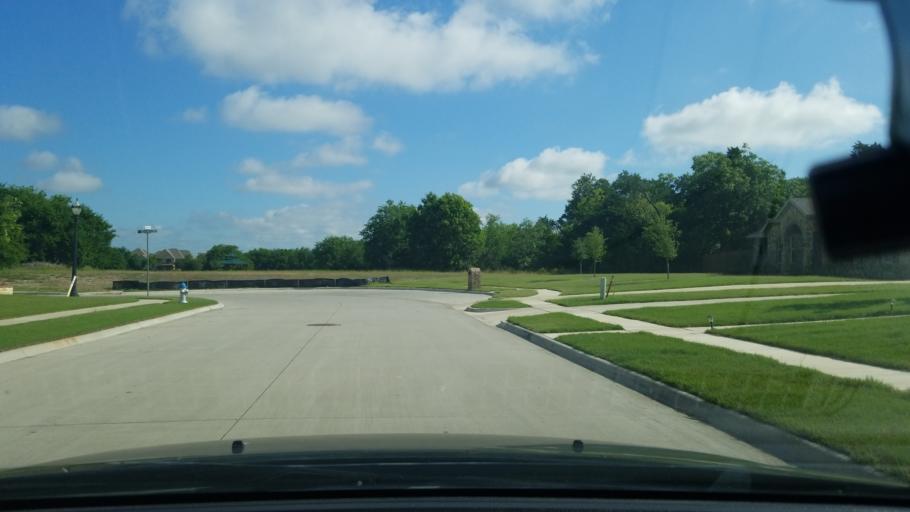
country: US
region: Texas
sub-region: Dallas County
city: Sunnyvale
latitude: 32.8025
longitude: -96.5618
